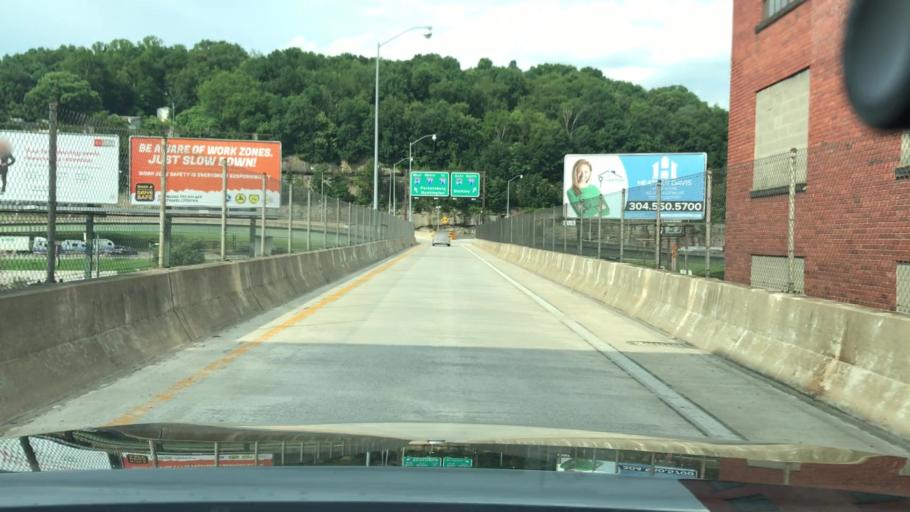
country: US
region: West Virginia
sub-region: Kanawha County
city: Charleston
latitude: 38.3504
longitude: -81.6248
